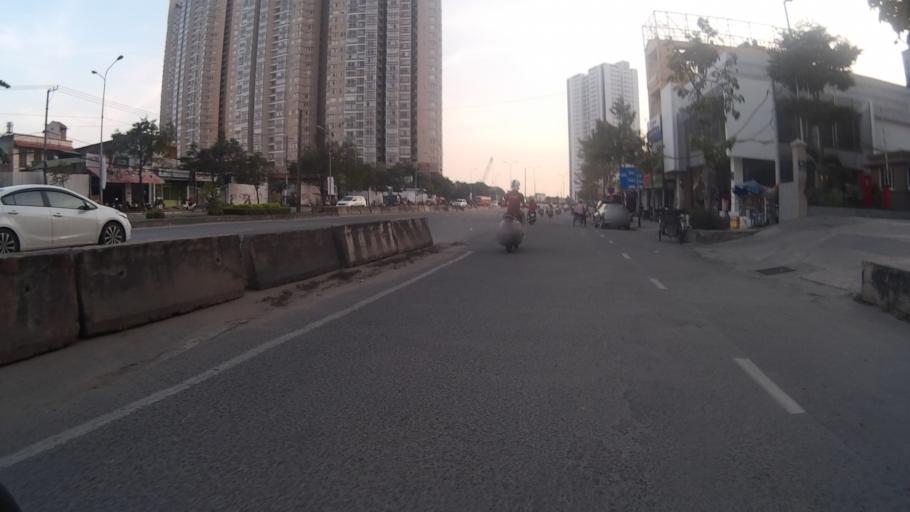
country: VN
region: Ho Chi Minh City
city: Quan Mot
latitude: 10.7927
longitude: 106.7180
